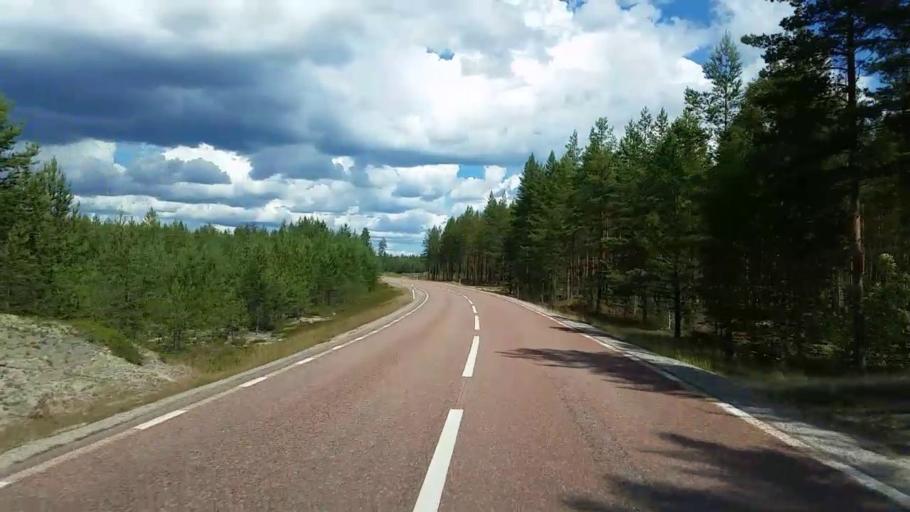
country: SE
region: Gaevleborg
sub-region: Ovanakers Kommun
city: Edsbyn
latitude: 61.3445
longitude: 15.5674
